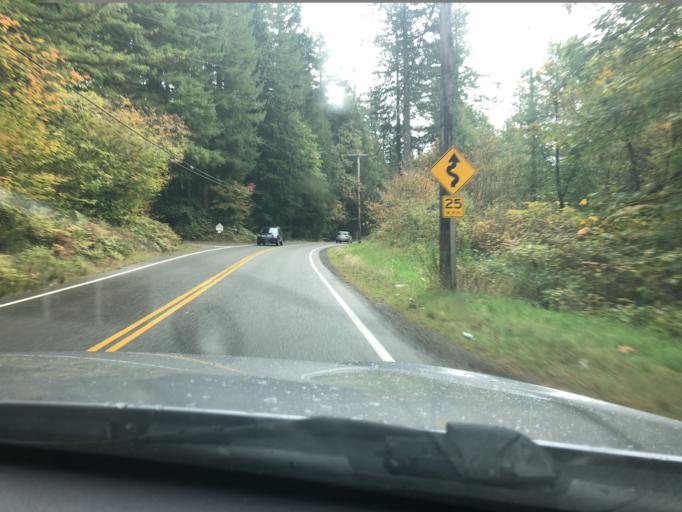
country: US
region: Washington
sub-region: King County
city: Riverbend
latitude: 47.4516
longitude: -121.7593
